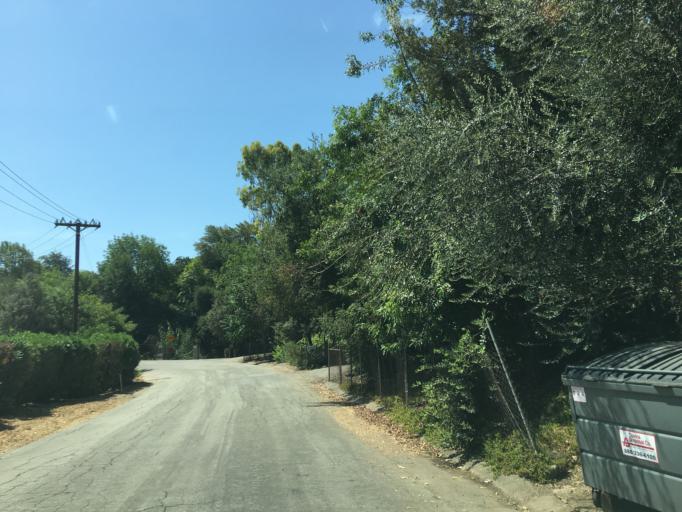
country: US
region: California
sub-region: Los Angeles County
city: Charter Oak
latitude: 34.0700
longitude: -117.8348
